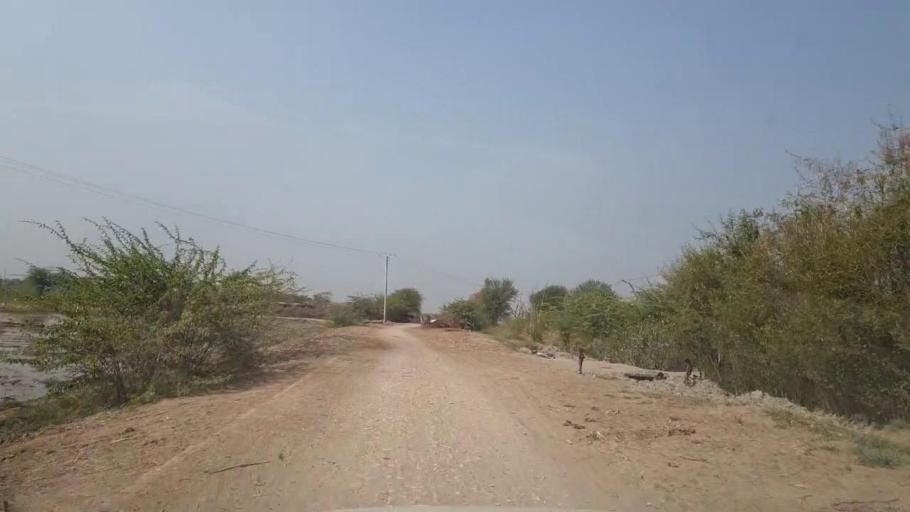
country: PK
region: Sindh
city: Mirpur Khas
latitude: 25.5690
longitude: 69.1415
